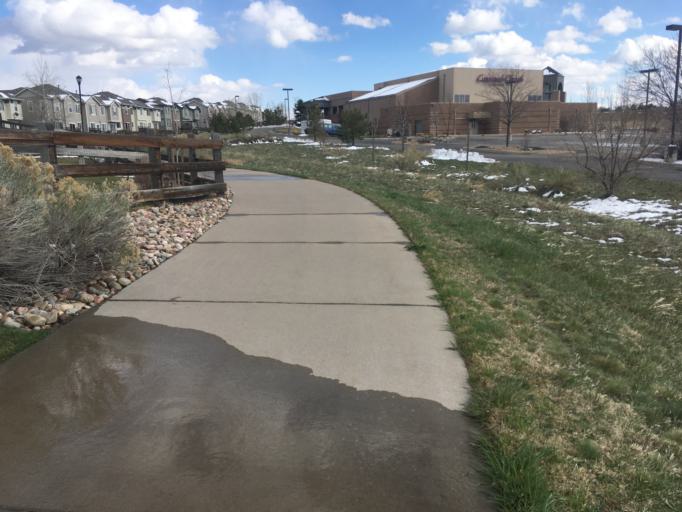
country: US
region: Colorado
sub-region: Adams County
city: Northglenn
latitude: 39.9323
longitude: -104.9862
